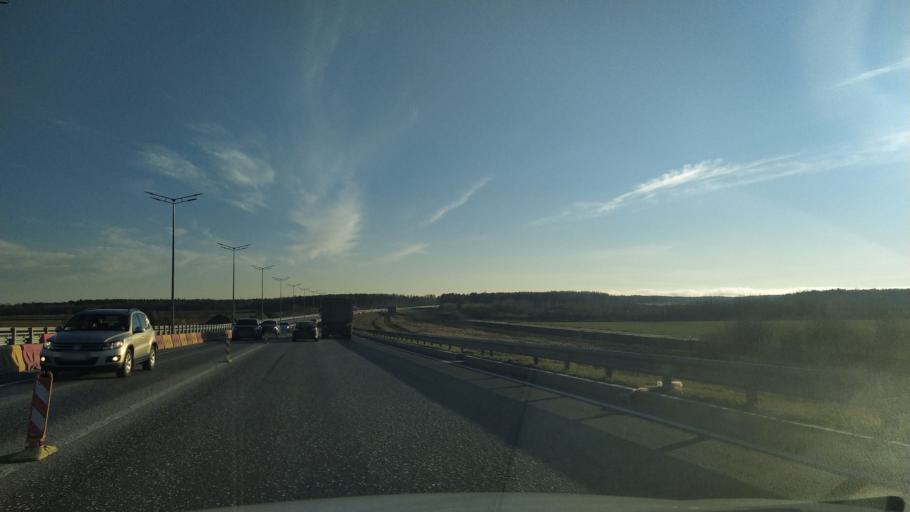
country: RU
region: St.-Petersburg
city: Levashovo
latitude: 60.0896
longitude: 30.2391
